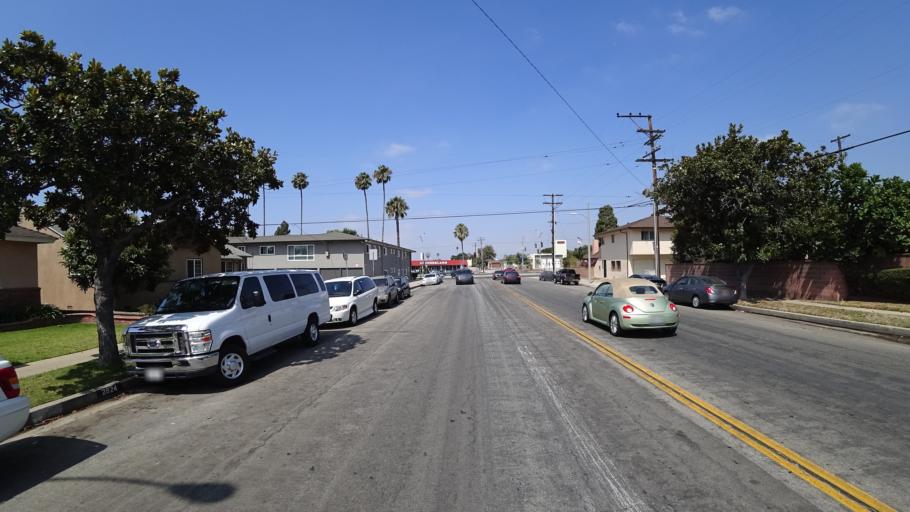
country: US
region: California
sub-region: Los Angeles County
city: Westmont
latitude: 33.9382
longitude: -118.3254
